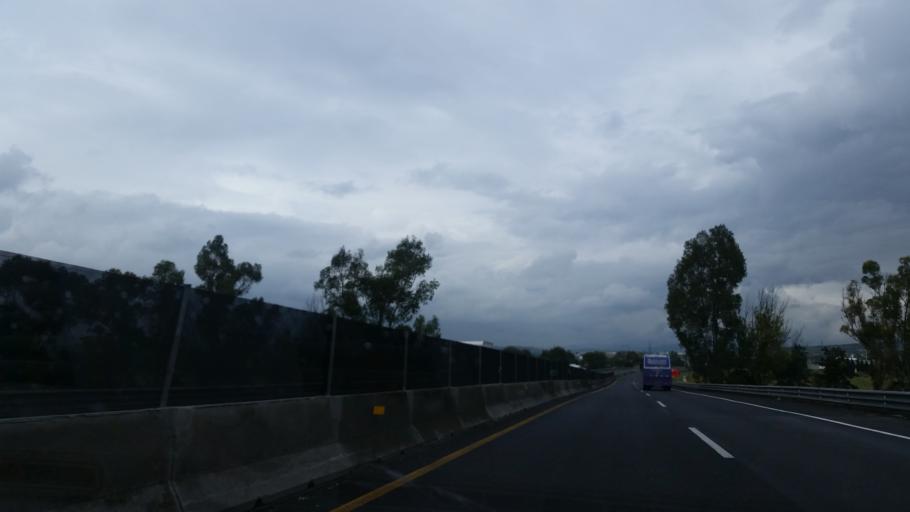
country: MX
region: Mexico
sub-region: Huehuetoca
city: Casa Nueva
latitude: 19.8201
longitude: -99.2057
